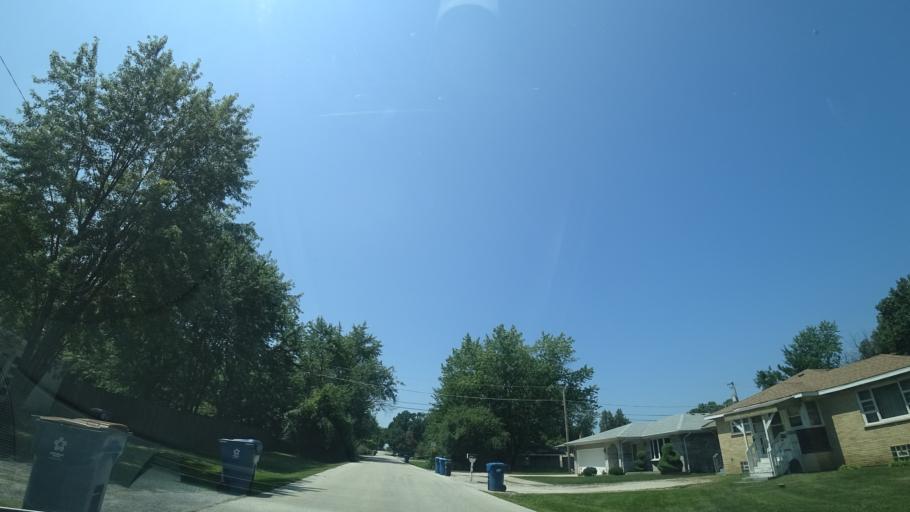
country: US
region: Illinois
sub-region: Cook County
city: Alsip
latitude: 41.6799
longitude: -87.7419
